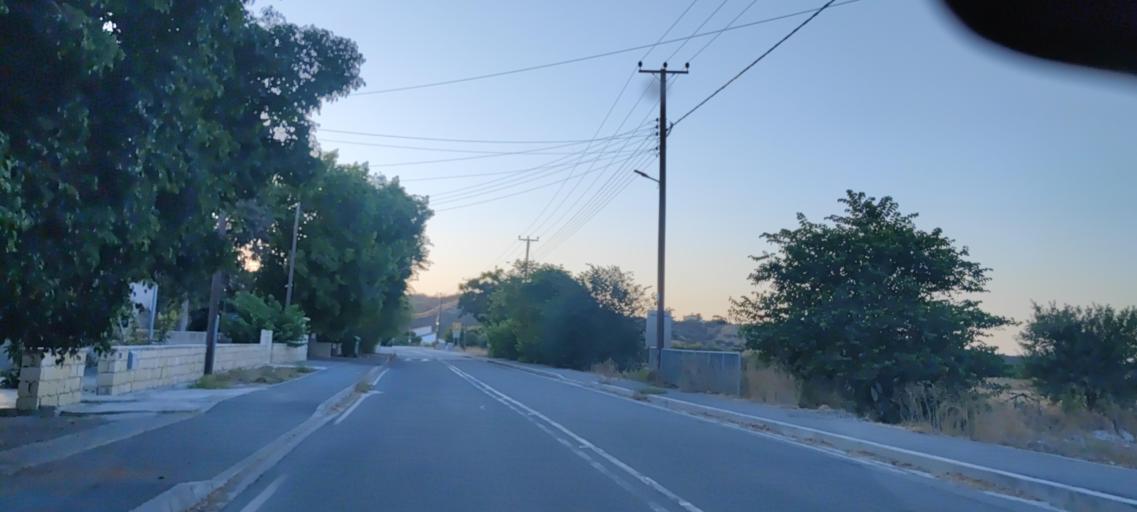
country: CY
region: Limassol
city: Sotira
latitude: 34.6763
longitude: 32.7935
